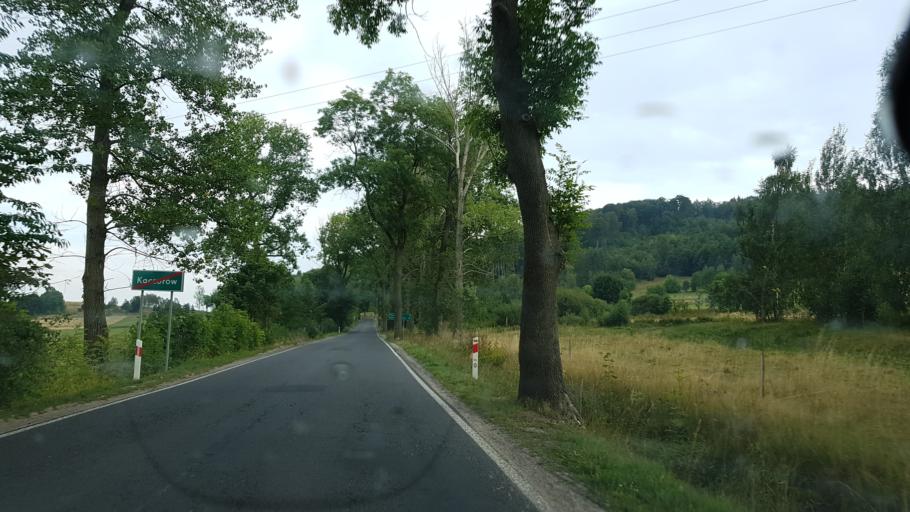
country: PL
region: Lower Silesian Voivodeship
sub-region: Powiat jeleniogorski
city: Janowice Wielkie
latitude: 50.9013
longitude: 15.9705
